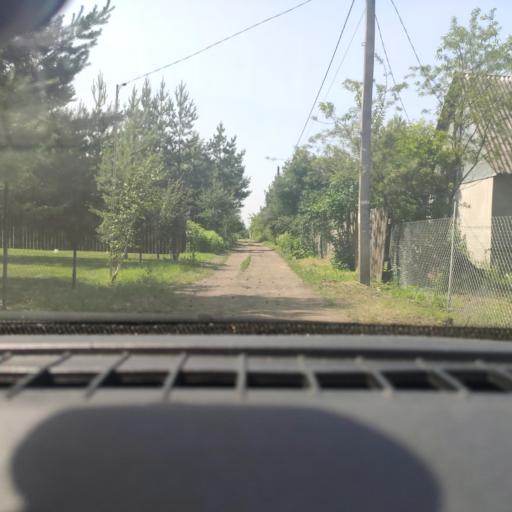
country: RU
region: Voronezj
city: Podgornoye
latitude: 51.8490
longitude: 39.2093
